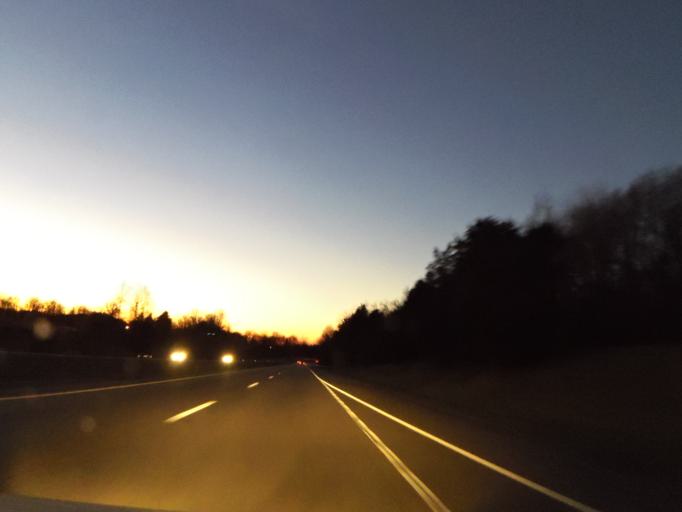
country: US
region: Tennessee
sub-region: Cocke County
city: Newport
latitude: 35.9722
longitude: -83.2643
